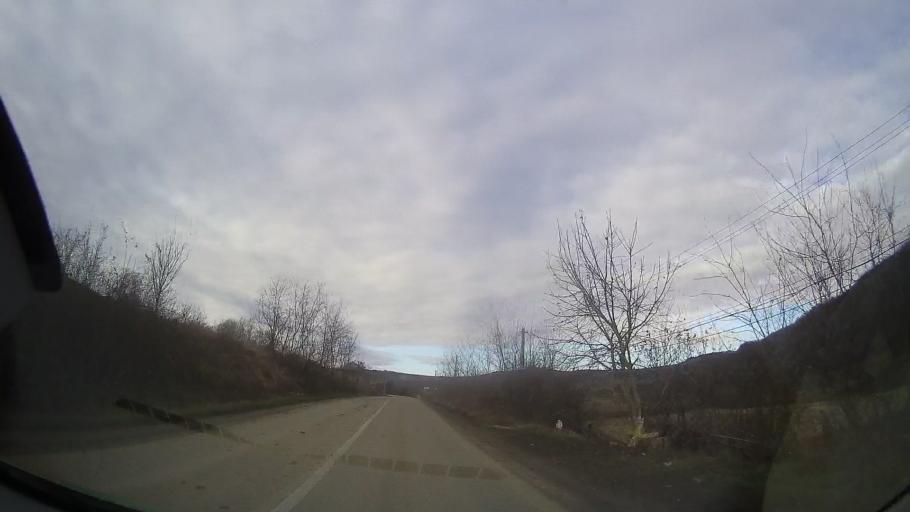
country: RO
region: Bistrita-Nasaud
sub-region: Comuna Micestii de Campie
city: Micestii de Campie
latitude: 46.8945
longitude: 24.2944
